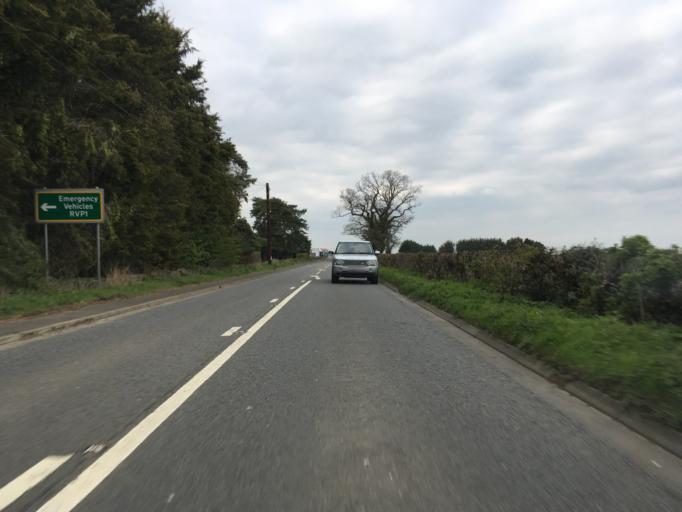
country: GB
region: England
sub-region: Wiltshire
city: Hankerton
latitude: 51.6611
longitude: -2.0523
